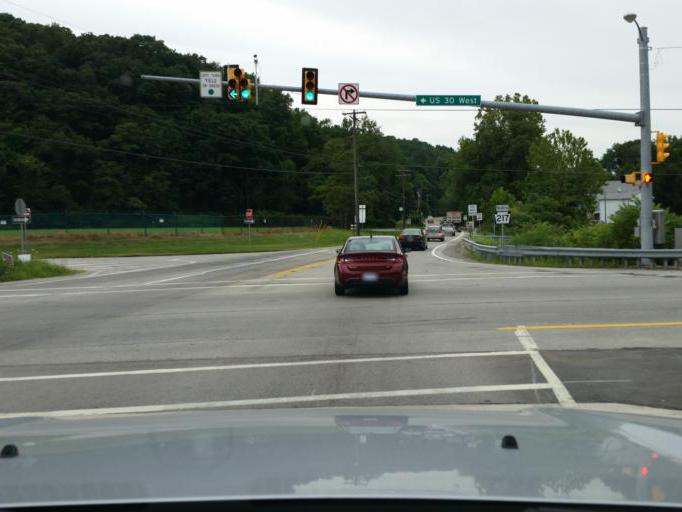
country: US
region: Pennsylvania
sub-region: Westmoreland County
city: Loyalhanna
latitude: 40.2920
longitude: -79.3410
